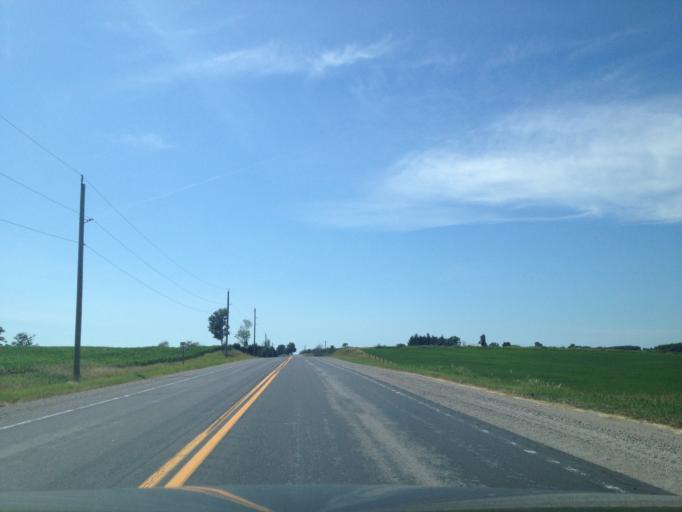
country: CA
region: Ontario
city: Stratford
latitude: 43.4861
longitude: -80.8400
